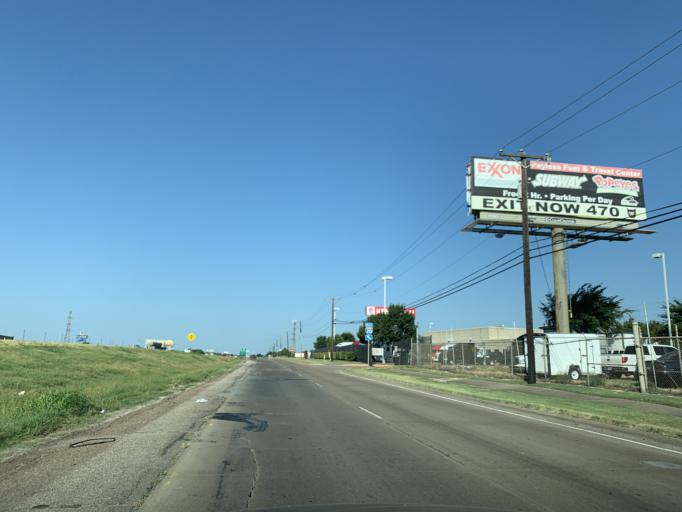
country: US
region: Texas
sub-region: Dallas County
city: Hutchins
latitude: 32.6541
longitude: -96.7582
